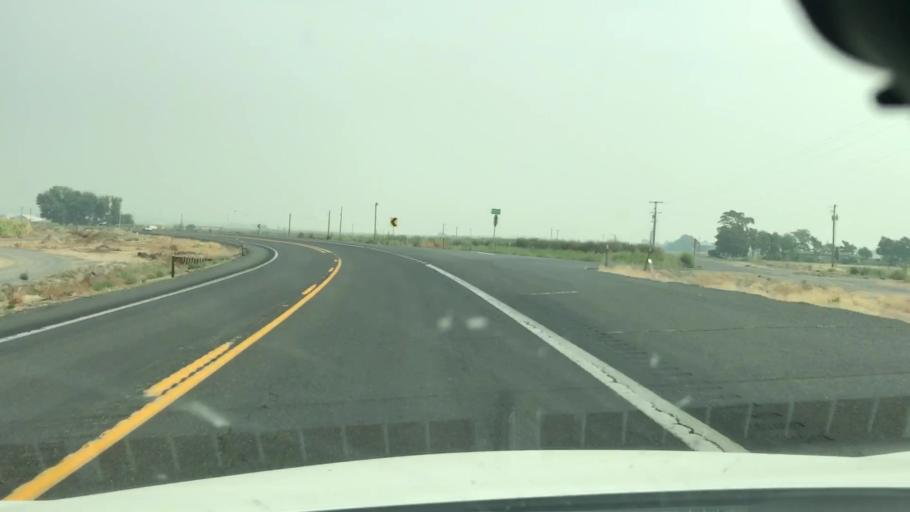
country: US
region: Washington
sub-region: Grant County
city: Quincy
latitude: 47.2345
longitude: -119.7472
